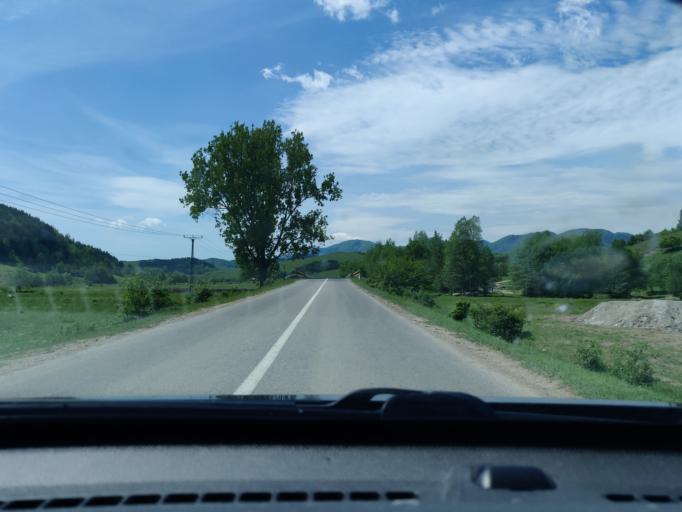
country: RO
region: Vrancea
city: Dragosloveni
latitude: 46.0136
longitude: 26.6835
